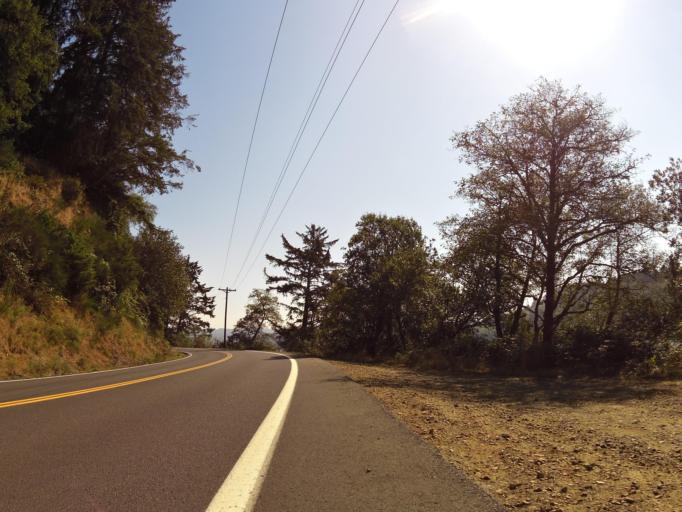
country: US
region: Oregon
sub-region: Tillamook County
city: Pacific City
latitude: 45.1821
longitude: -123.9448
